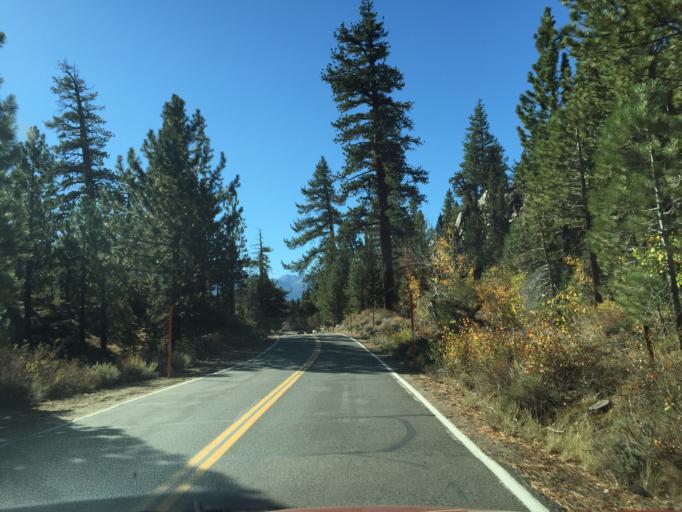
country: US
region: California
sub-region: Mono County
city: Bridgeport
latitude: 38.3318
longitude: -119.5537
